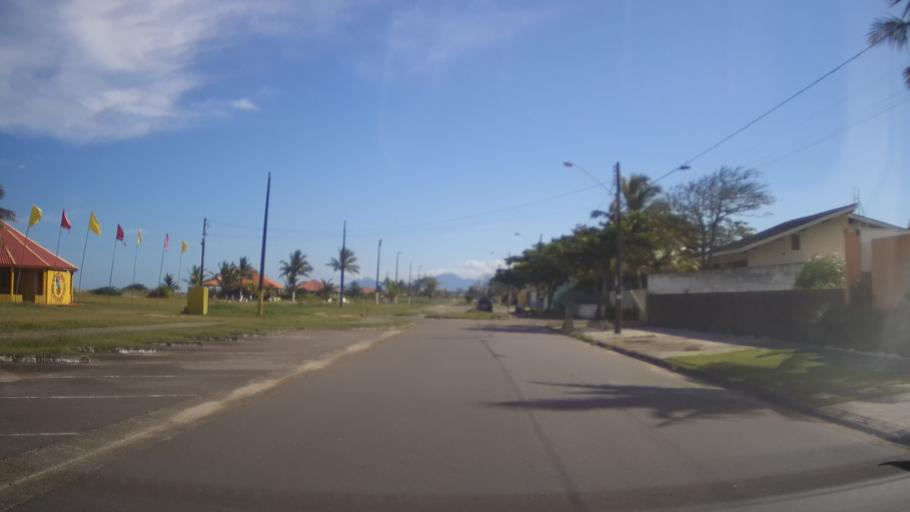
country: BR
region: Sao Paulo
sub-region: Itanhaem
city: Itanhaem
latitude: -24.2073
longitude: -46.8293
